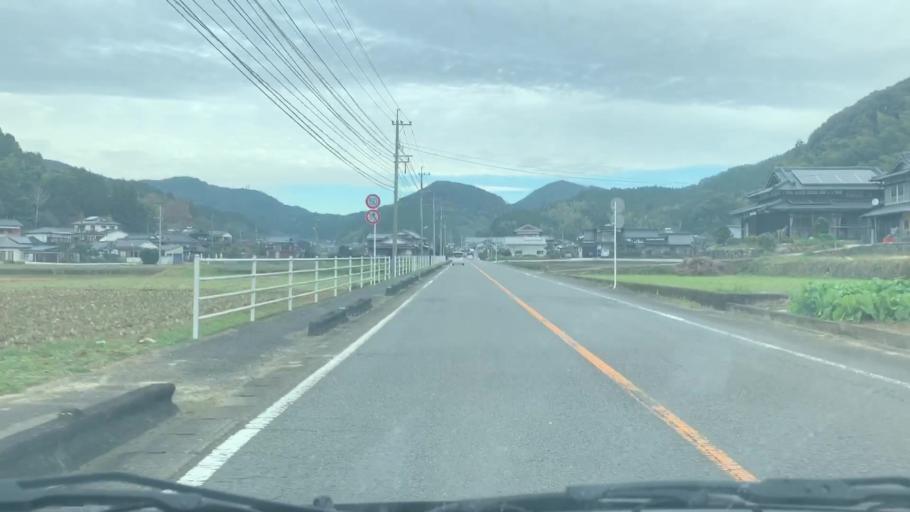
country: JP
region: Saga Prefecture
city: Ureshinomachi-shimojuku
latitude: 33.1434
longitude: 129.9765
